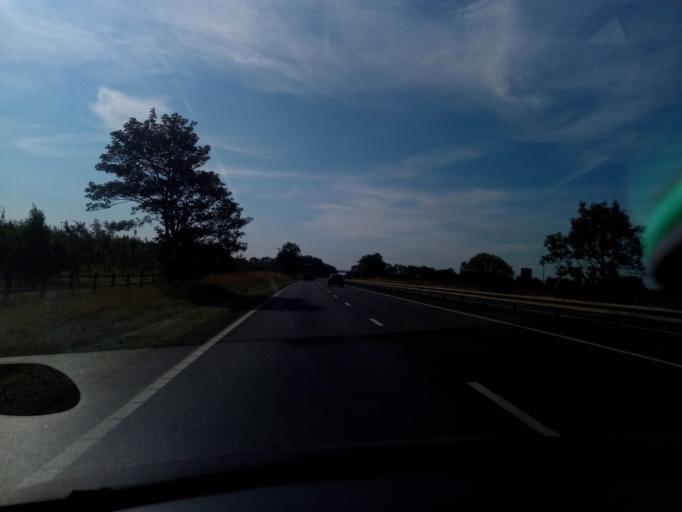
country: GB
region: England
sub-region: Redcar and Cleveland
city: Thornaby-on-Tees
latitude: 54.5030
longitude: -1.2914
